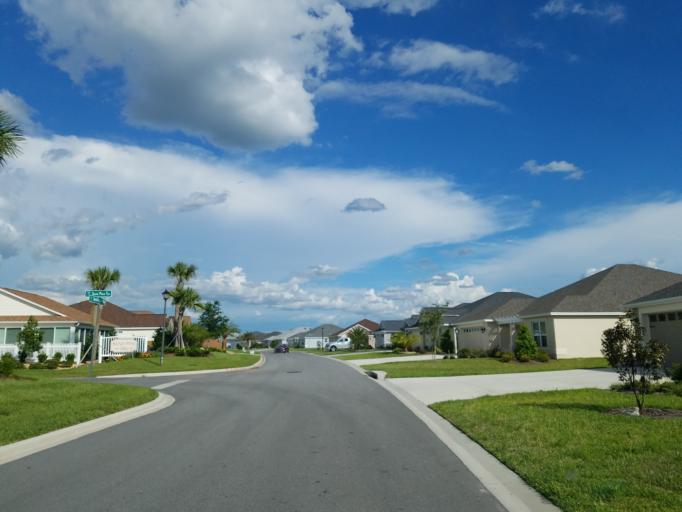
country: US
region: Florida
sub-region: Sumter County
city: Wildwood
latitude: 28.7951
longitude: -82.0343
